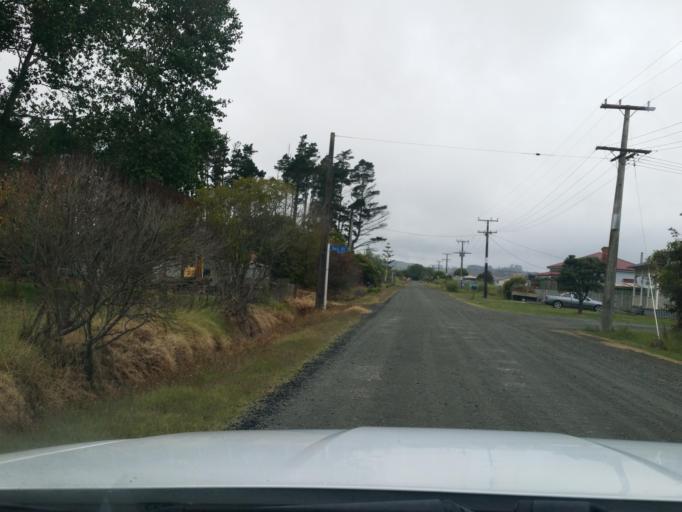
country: NZ
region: Northland
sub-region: Kaipara District
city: Dargaville
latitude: -36.0145
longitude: 173.9032
